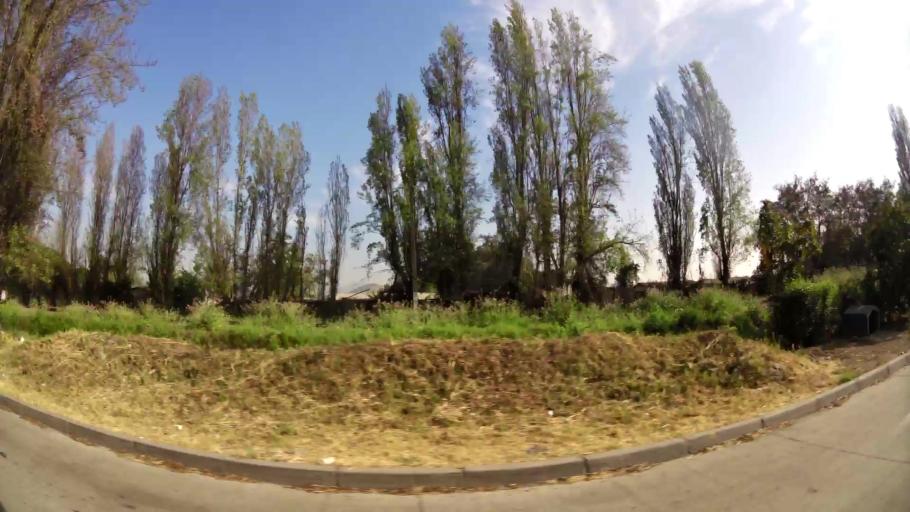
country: CL
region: Santiago Metropolitan
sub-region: Provincia de Talagante
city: Penaflor
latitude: -33.5548
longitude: -70.7970
